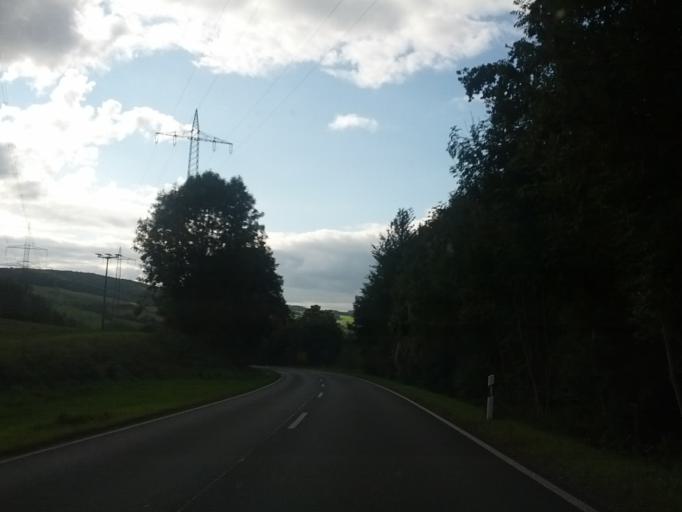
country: DE
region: Thuringia
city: Krauthausen
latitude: 51.0177
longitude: 10.2444
